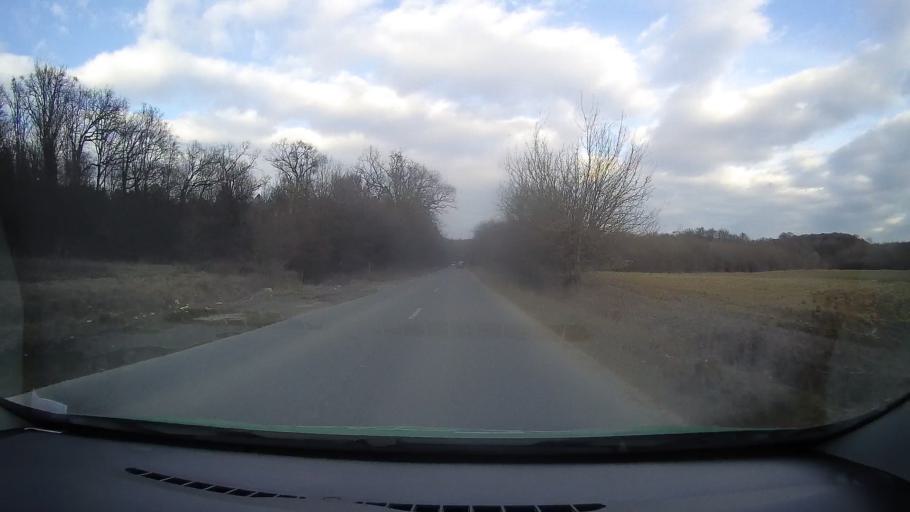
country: RO
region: Dambovita
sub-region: Comuna Gura Ocnitei
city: Gura Ocnitei
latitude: 44.9489
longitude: 25.5925
